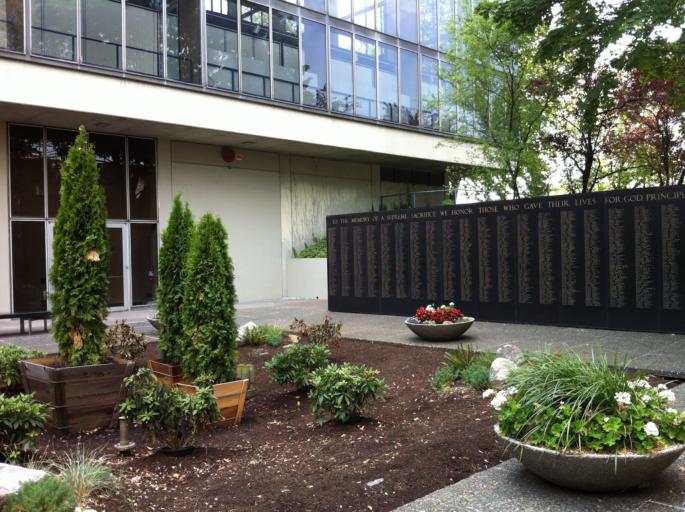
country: US
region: Oregon
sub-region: Multnomah County
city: Portland
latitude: 45.5327
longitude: -122.6690
